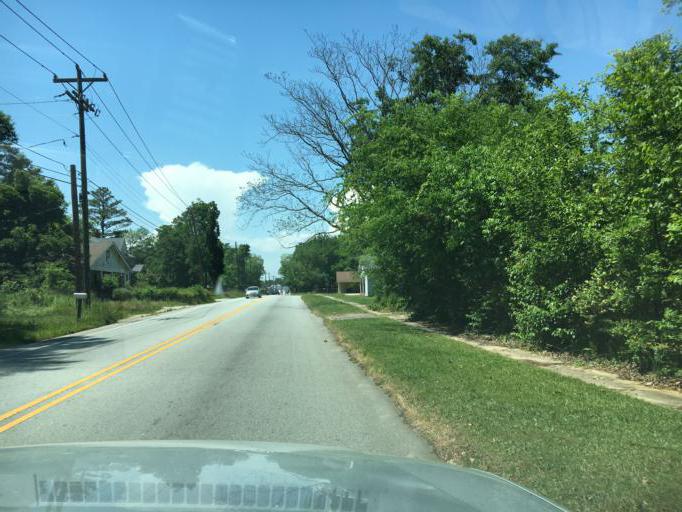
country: US
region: South Carolina
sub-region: Spartanburg County
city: Saxon
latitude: 34.9666
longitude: -81.9590
